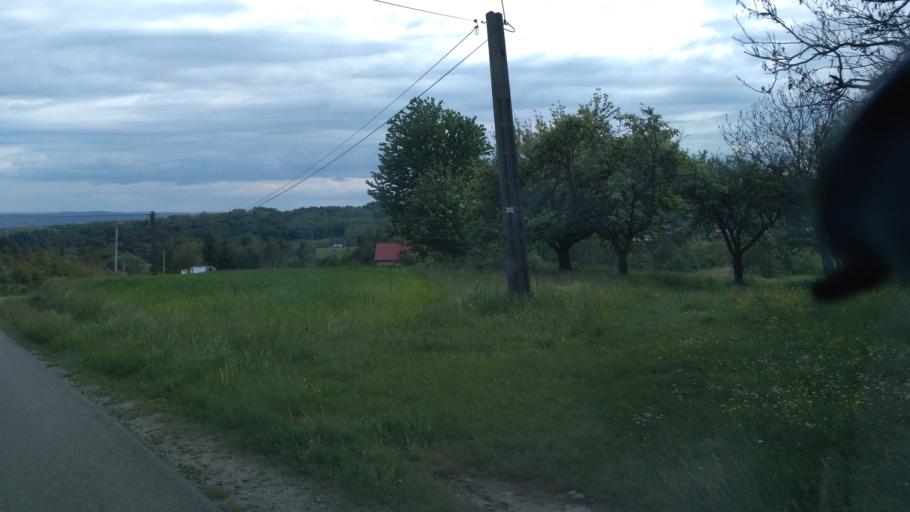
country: PL
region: Subcarpathian Voivodeship
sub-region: Powiat przemyski
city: Nienadowa
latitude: 49.8786
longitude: 22.4174
